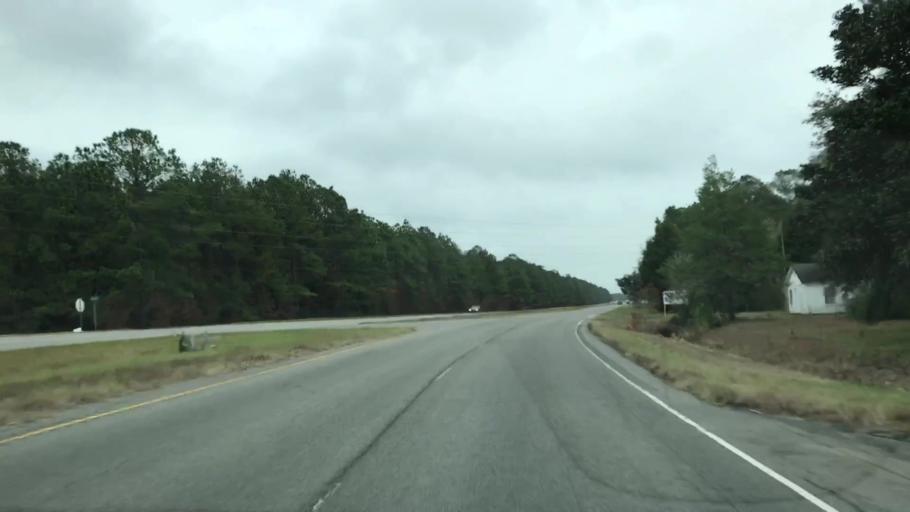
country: US
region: South Carolina
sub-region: Charleston County
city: Awendaw
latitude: 33.0375
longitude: -79.6152
